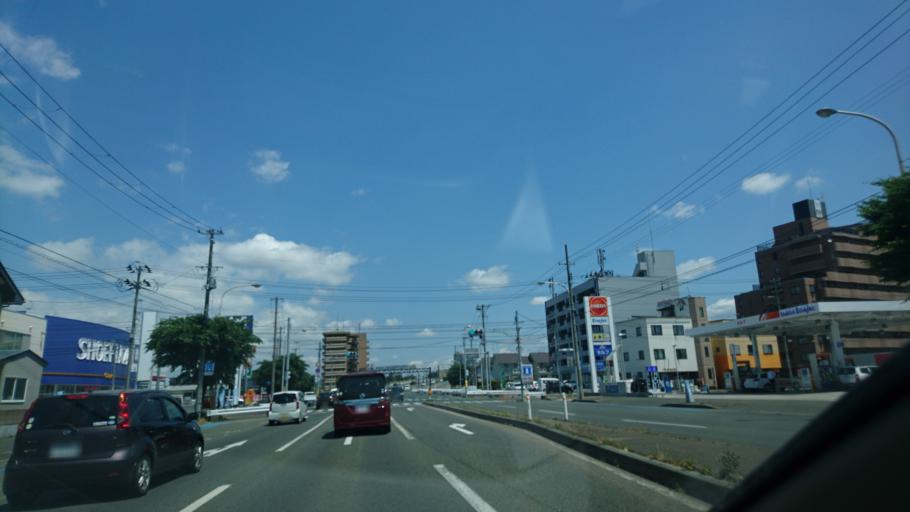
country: JP
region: Iwate
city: Morioka-shi
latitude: 39.6881
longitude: 141.1356
